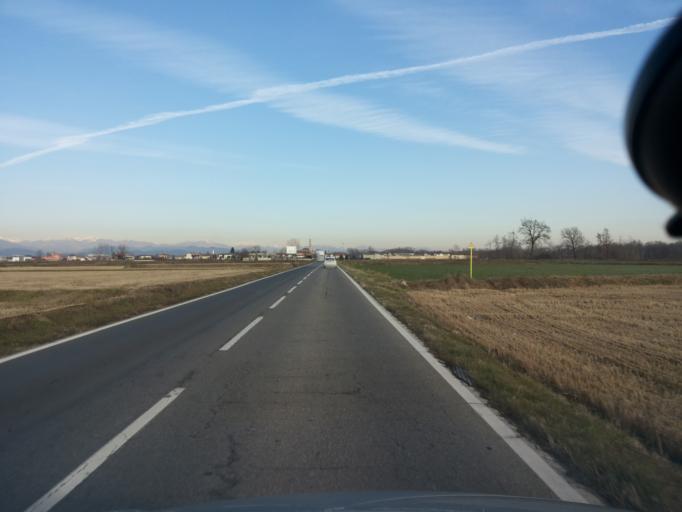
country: IT
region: Piedmont
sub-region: Provincia di Vercelli
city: Arborio
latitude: 45.4846
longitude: 8.3885
